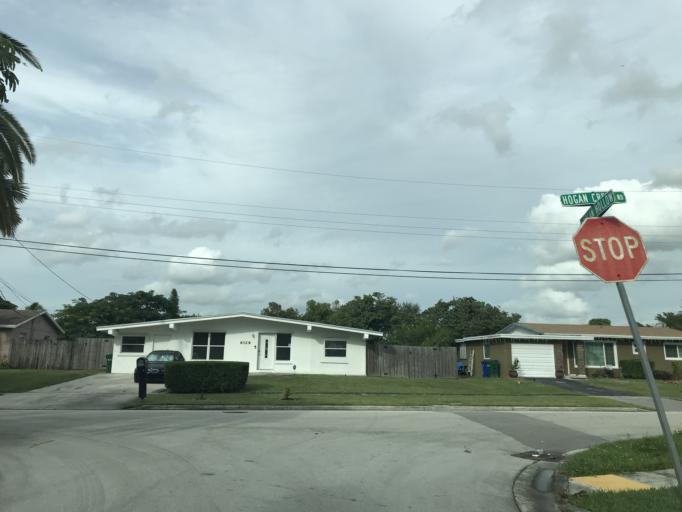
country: US
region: Florida
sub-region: Broward County
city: Margate
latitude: 26.2565
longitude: -80.2064
